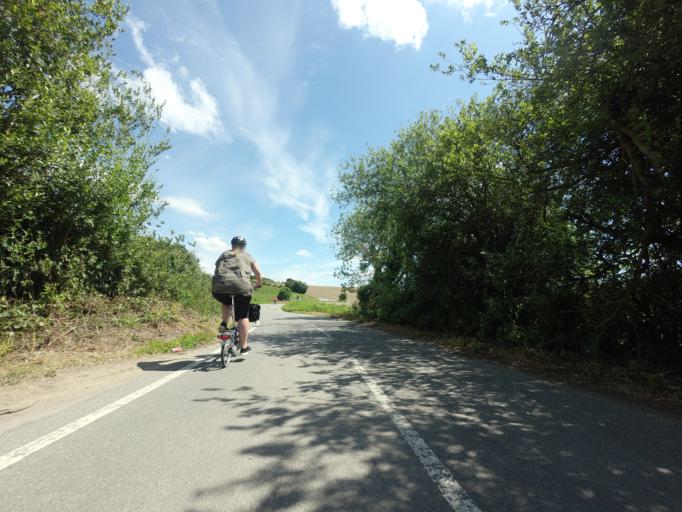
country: GB
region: England
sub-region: Medway
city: High Halstow
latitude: 51.4526
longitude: 0.5449
